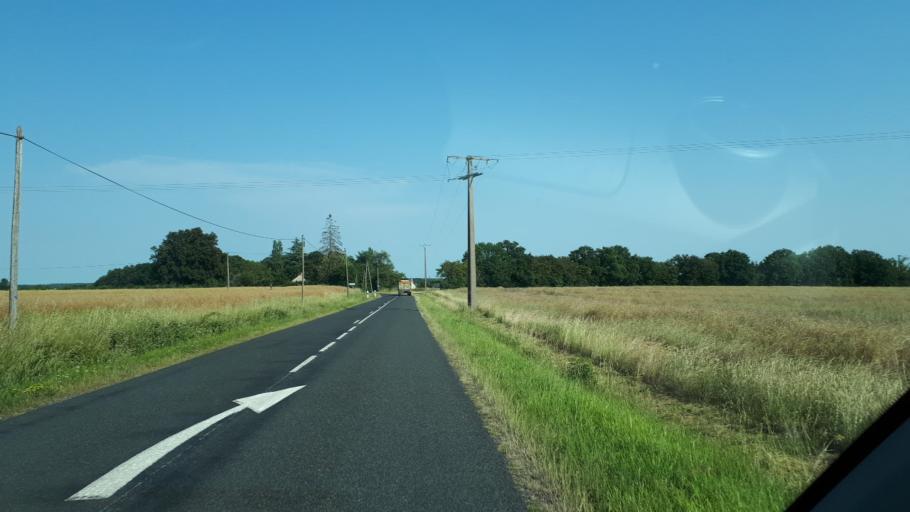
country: FR
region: Centre
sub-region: Departement du Loir-et-Cher
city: La Ville-aux-Clercs
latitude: 47.9653
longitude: 1.0620
